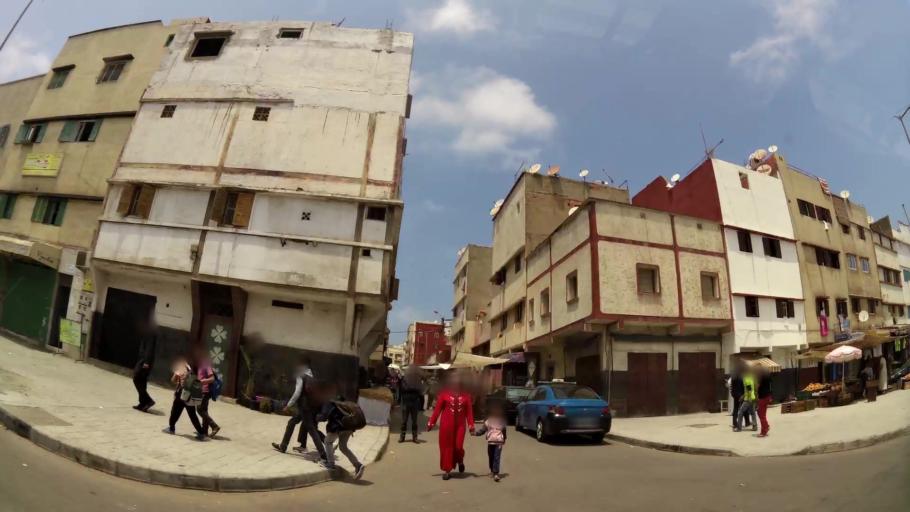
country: MA
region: Rabat-Sale-Zemmour-Zaer
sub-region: Rabat
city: Rabat
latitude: 33.9842
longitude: -6.8790
